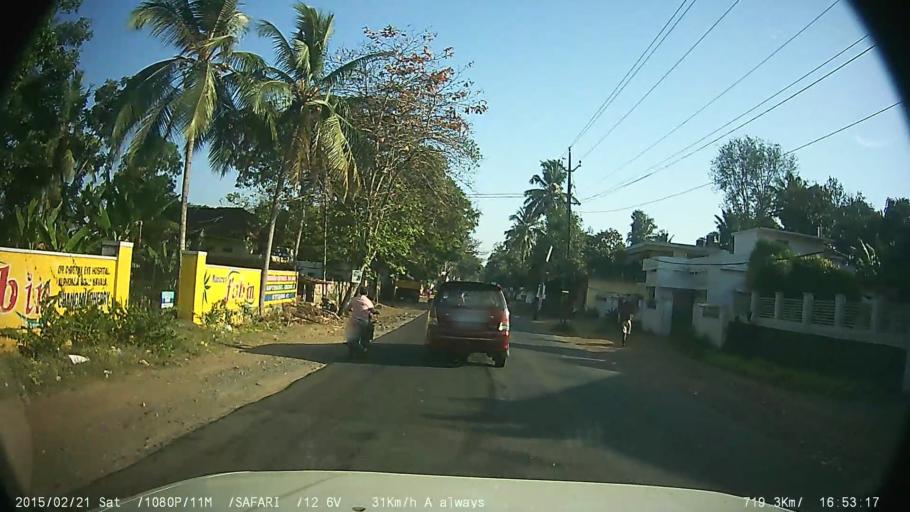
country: IN
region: Kerala
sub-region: Kottayam
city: Changanacheri
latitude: 9.4769
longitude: 76.5279
